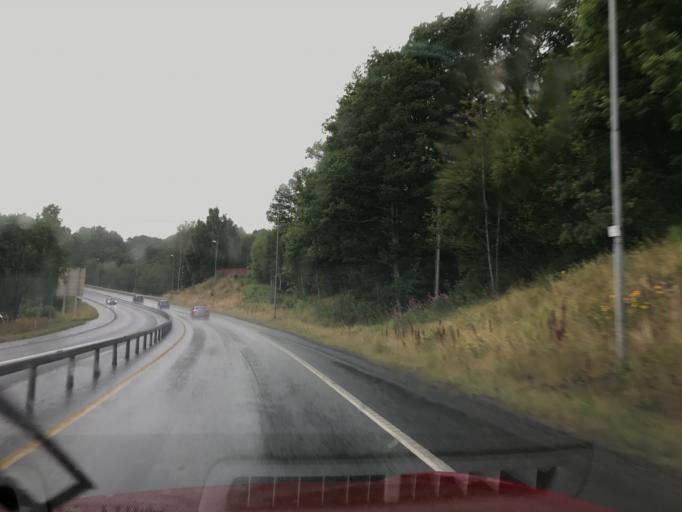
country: NO
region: Aust-Agder
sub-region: Grimstad
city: Grimstad
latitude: 58.3697
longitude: 8.6103
